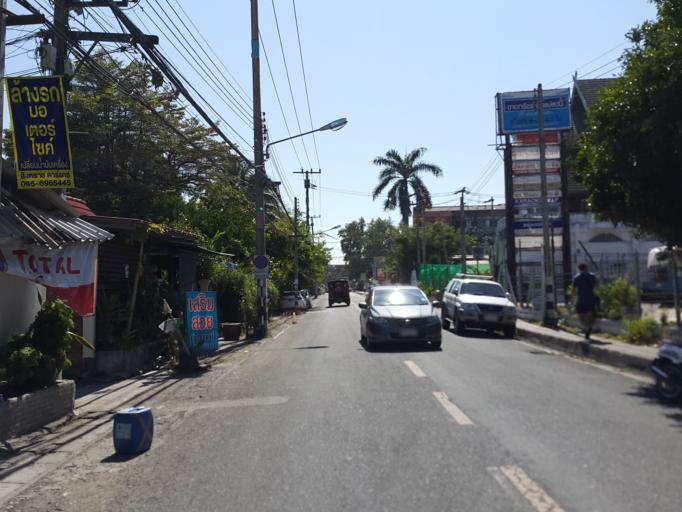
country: TH
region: Chiang Mai
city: Chiang Mai
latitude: 18.7947
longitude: 98.9818
